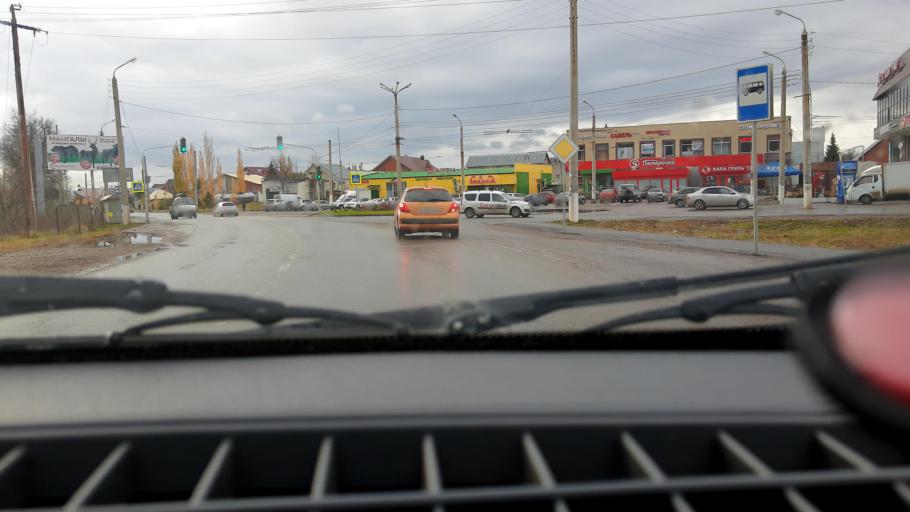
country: RU
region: Bashkortostan
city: Ufa
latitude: 54.7898
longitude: 55.9502
